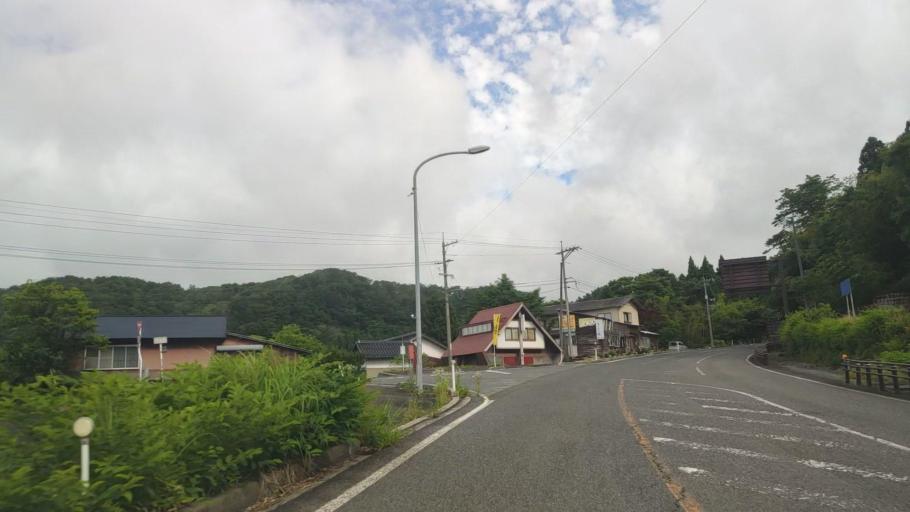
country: JP
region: Tottori
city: Yonago
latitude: 35.3236
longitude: 133.5570
